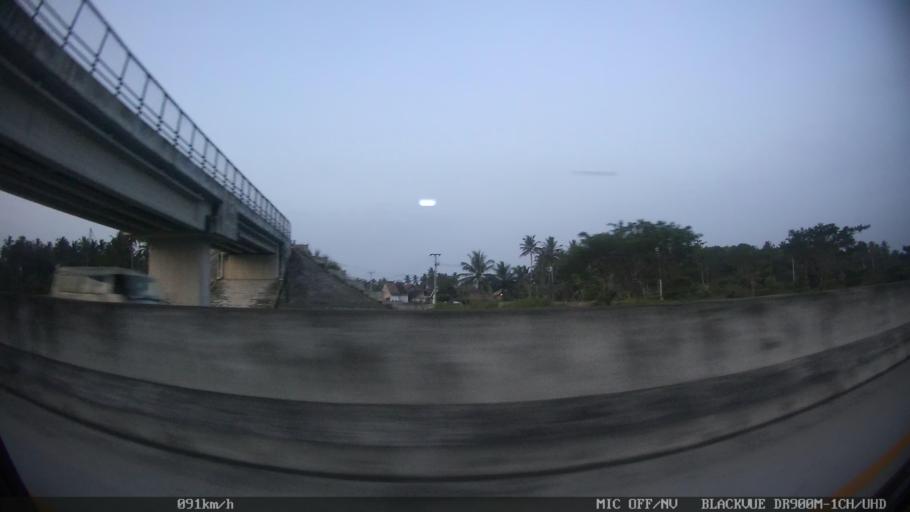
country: ID
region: Lampung
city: Sidorejo
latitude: -5.6491
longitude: 105.5810
